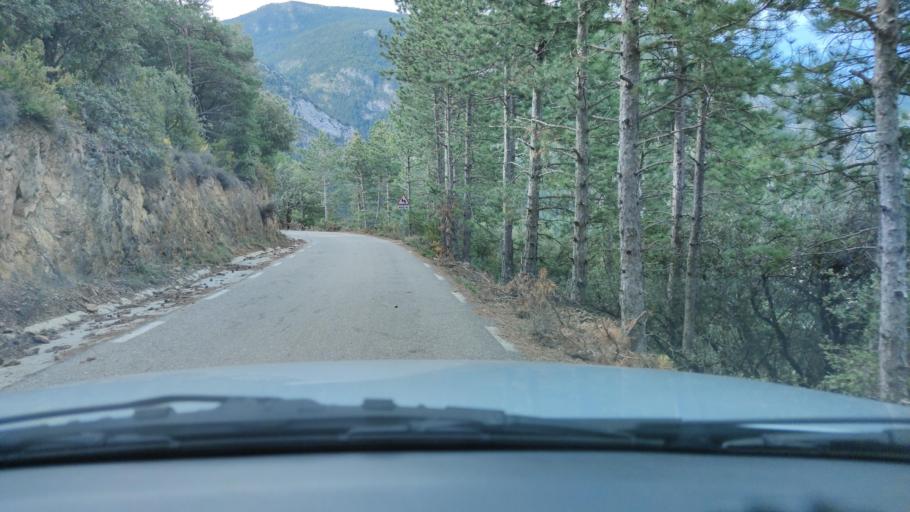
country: ES
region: Catalonia
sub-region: Provincia de Lleida
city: la Seu d'Urgell
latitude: 42.2422
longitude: 1.4254
